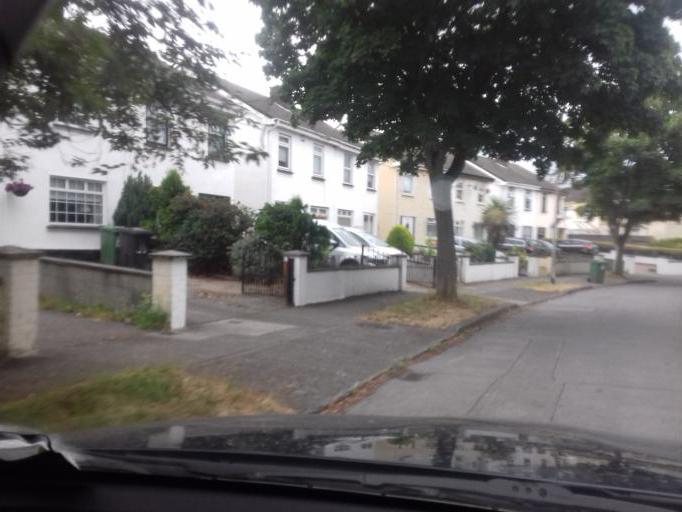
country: IE
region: Leinster
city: Hartstown
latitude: 53.3943
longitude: -6.4101
